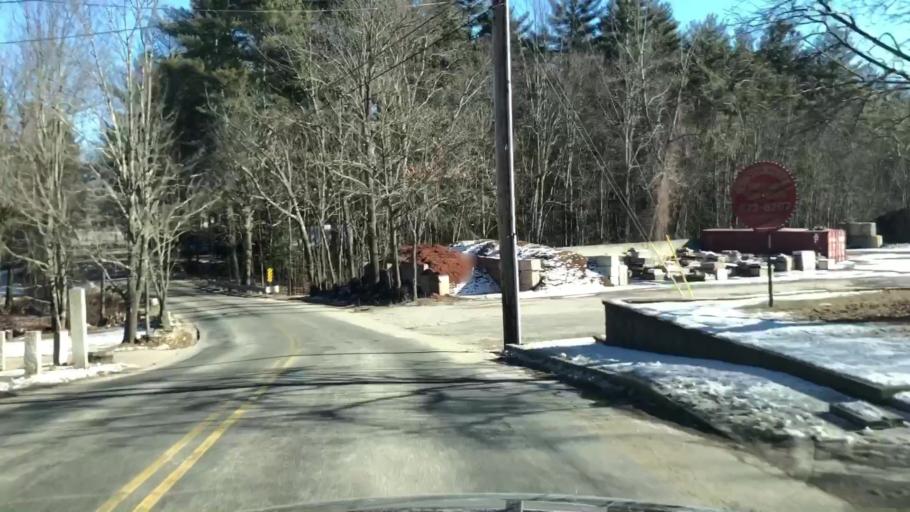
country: US
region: New Hampshire
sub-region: Hillsborough County
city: Milford
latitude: 42.8161
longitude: -71.6557
